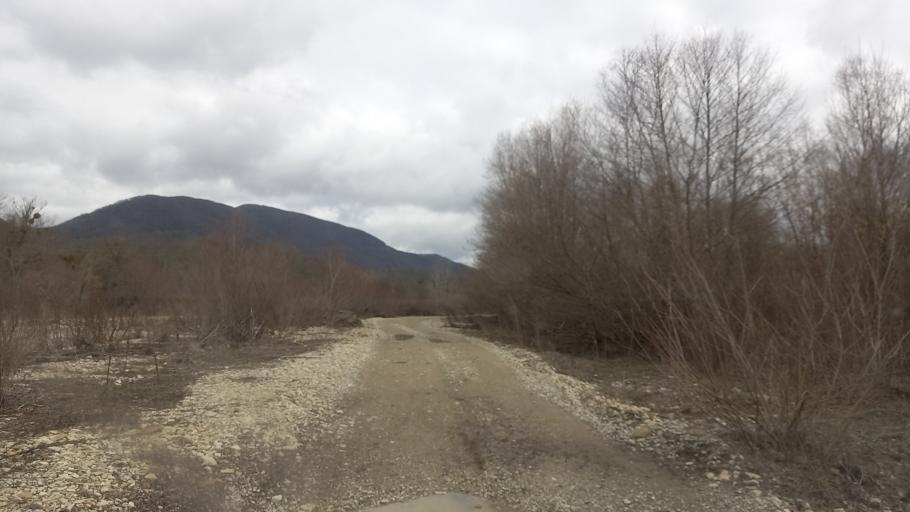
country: RU
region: Krasnodarskiy
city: Pshada
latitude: 44.4899
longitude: 38.4125
